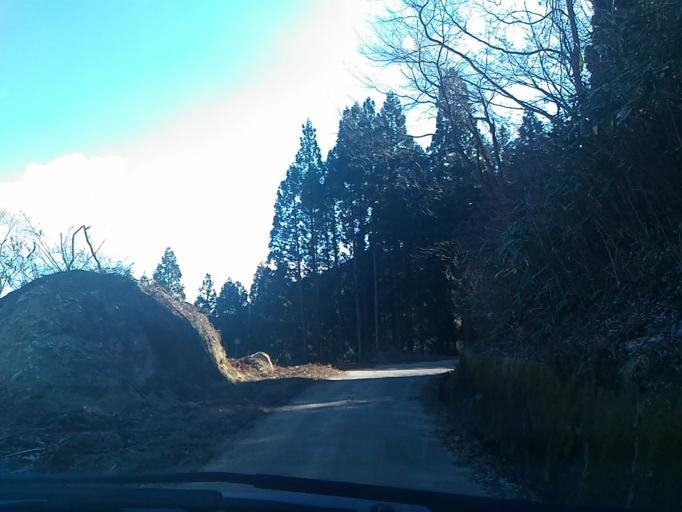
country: JP
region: Fukushima
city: Ishikawa
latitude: 37.0437
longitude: 140.5995
